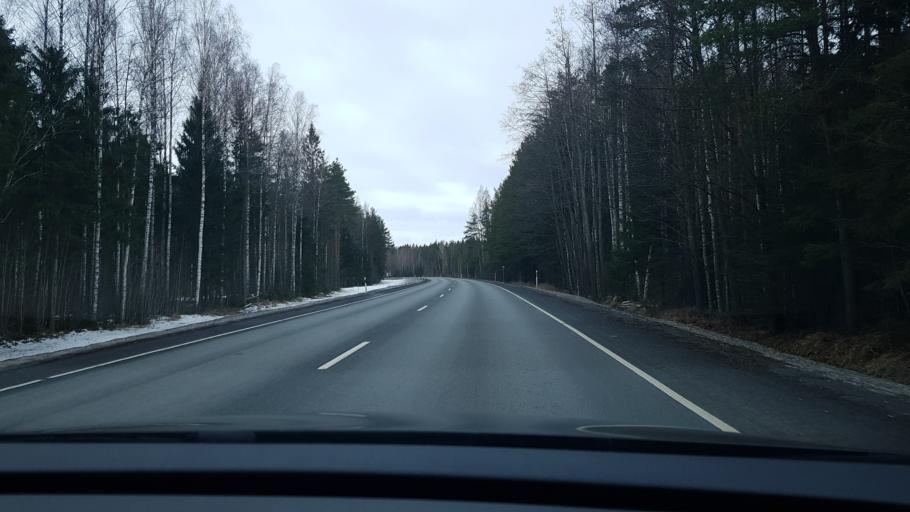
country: EE
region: Paernumaa
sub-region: Paikuse vald
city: Paikuse
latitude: 58.2520
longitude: 24.6842
